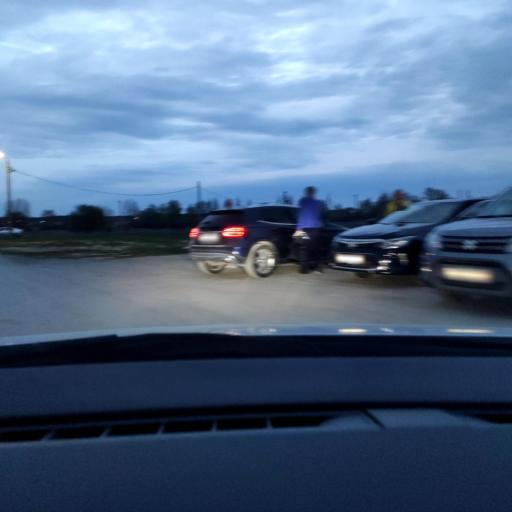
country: RU
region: Lipetsk
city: Donskoye
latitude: 52.6770
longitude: 38.9152
